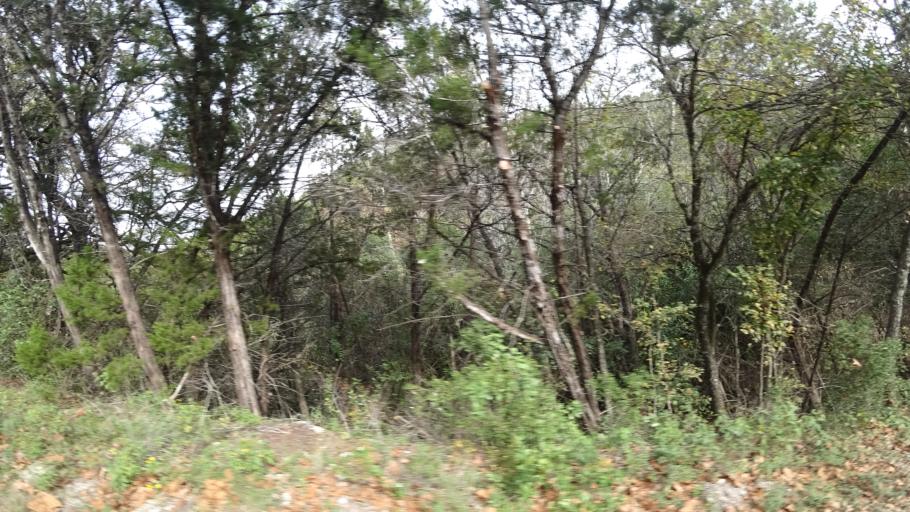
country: US
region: Texas
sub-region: Travis County
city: Hudson Bend
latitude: 30.3876
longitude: -97.9243
